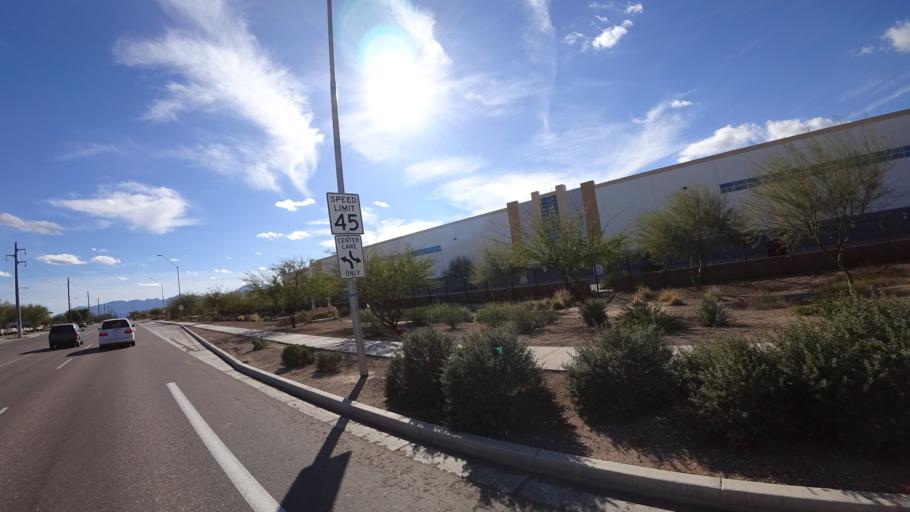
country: US
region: Arizona
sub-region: Maricopa County
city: Tolleson
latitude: 33.4356
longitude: -112.2212
